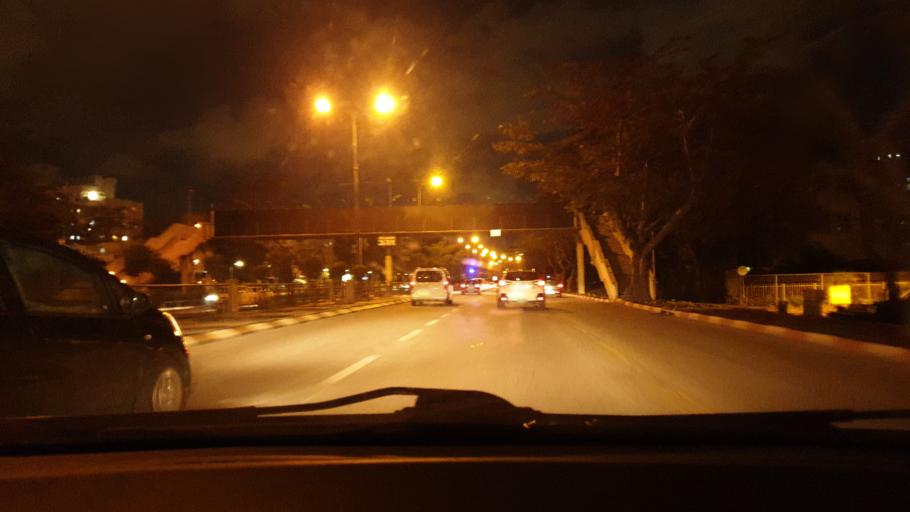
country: IL
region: Central District
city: Rishon LeZiyyon
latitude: 31.9556
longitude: 34.8025
